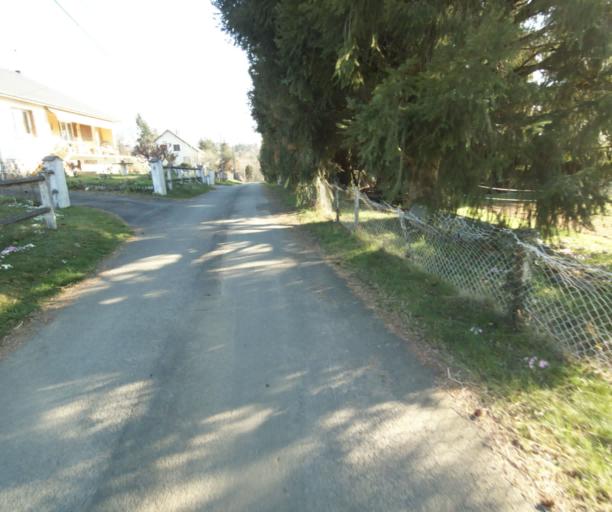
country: FR
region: Limousin
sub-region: Departement de la Correze
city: Saint-Clement
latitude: 45.3404
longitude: 1.6737
